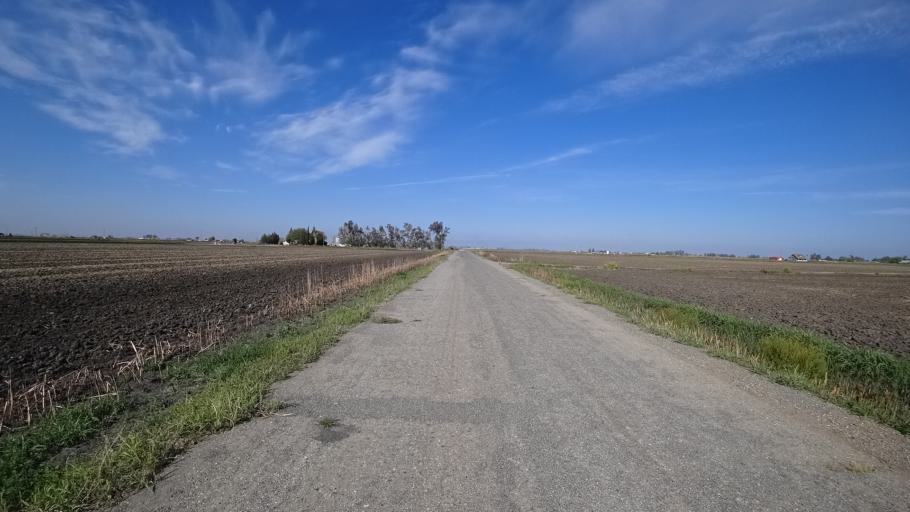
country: US
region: California
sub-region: Glenn County
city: Willows
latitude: 39.5726
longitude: -122.0435
